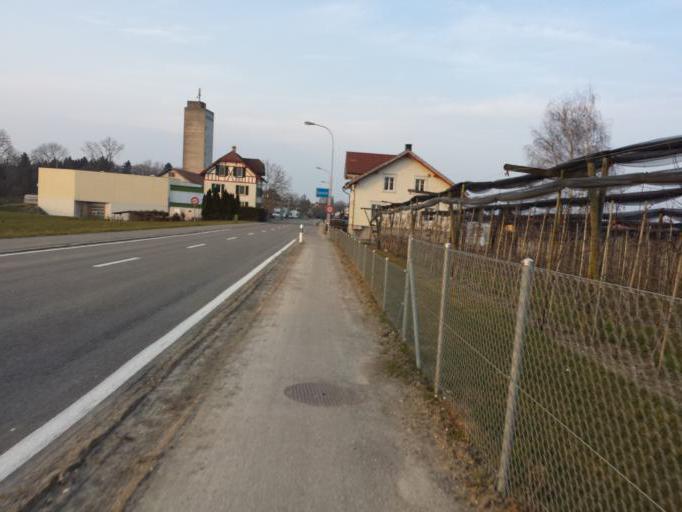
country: CH
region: Thurgau
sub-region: Arbon District
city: Egnach
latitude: 47.5362
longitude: 9.3751
